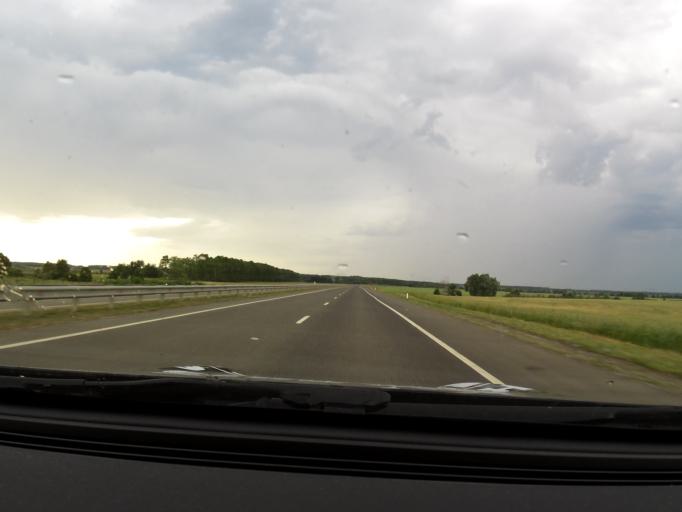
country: RU
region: Bashkortostan
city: Kushnarenkovo
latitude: 55.0610
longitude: 55.3965
